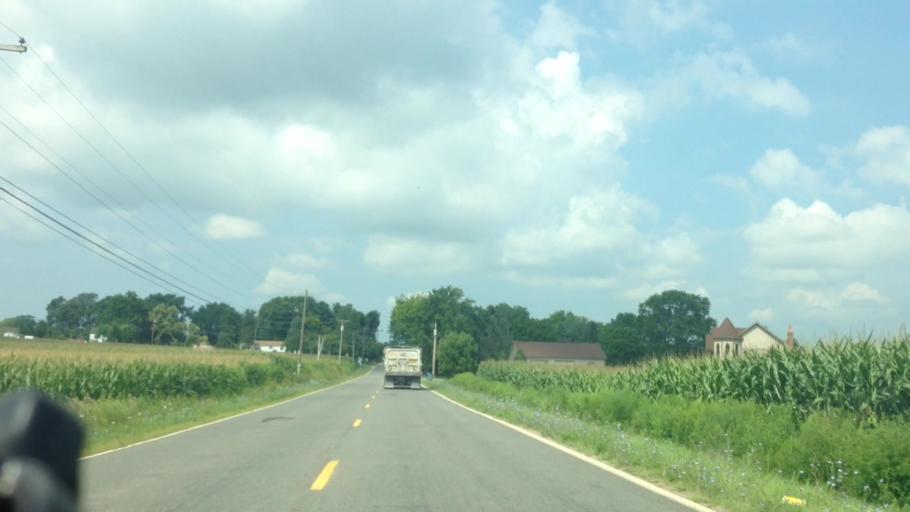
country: US
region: Ohio
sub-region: Stark County
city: Canal Fulton
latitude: 40.8537
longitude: -81.6443
